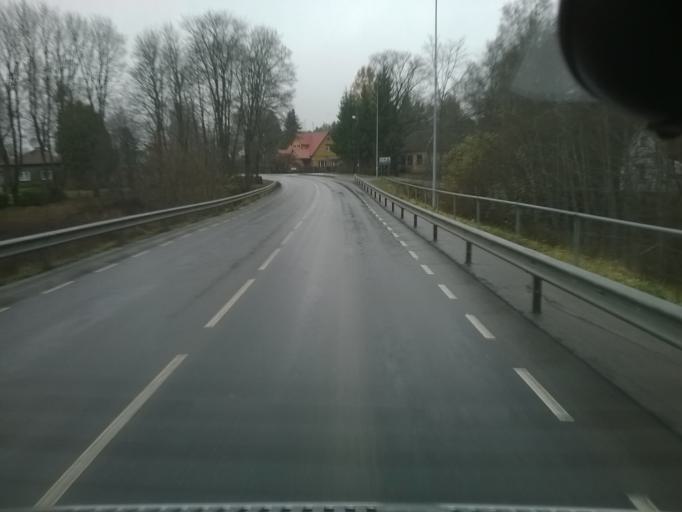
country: EE
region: Harju
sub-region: Saku vald
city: Saku
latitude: 59.2345
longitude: 24.6826
